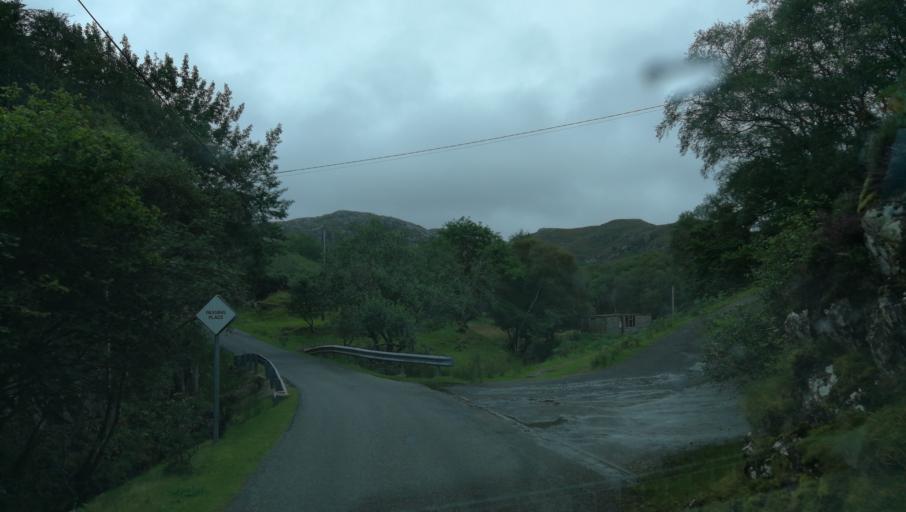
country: GB
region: Scotland
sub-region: Highland
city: Ullapool
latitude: 58.1366
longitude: -5.2553
